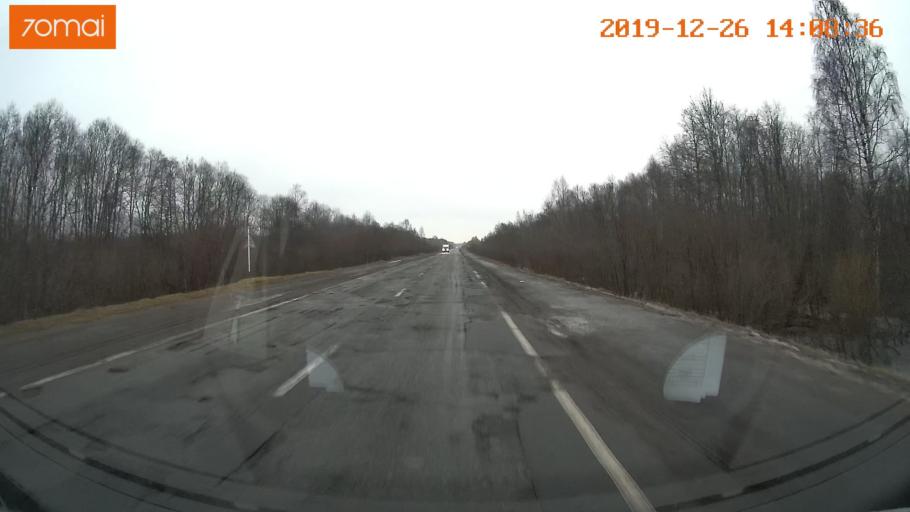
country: RU
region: Jaroslavl
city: Poshekhon'ye
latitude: 58.5087
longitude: 38.9157
